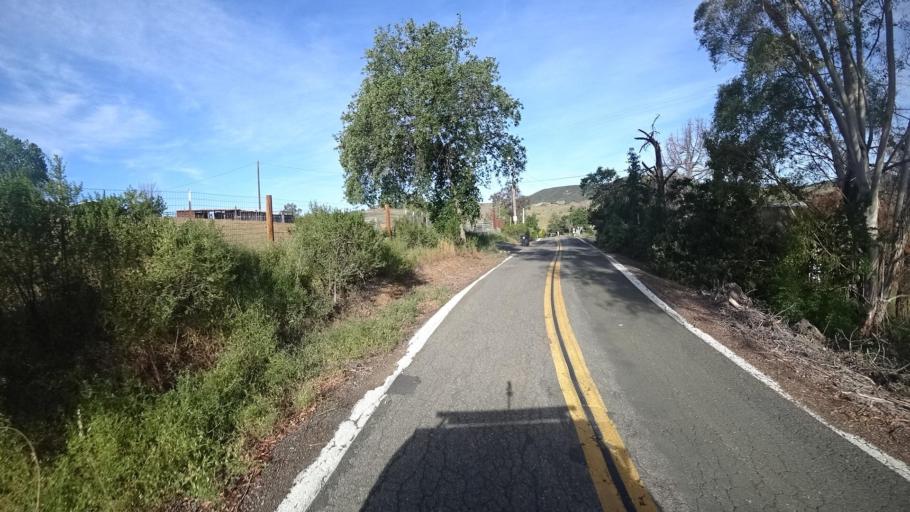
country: US
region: California
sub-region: Lake County
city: North Lakeport
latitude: 39.0984
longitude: -122.9144
